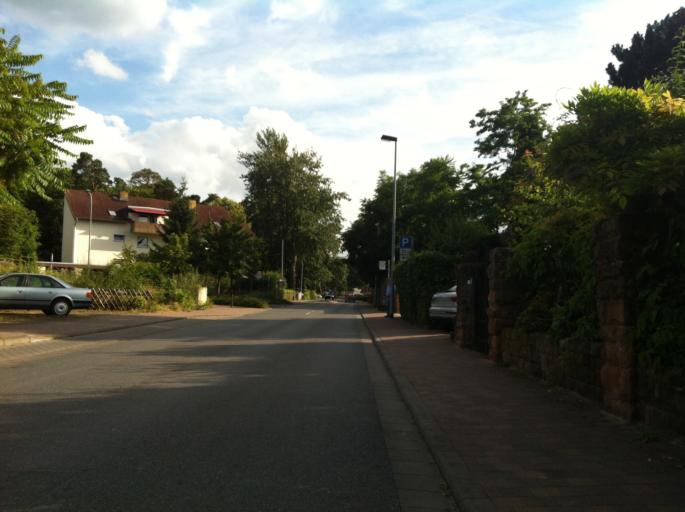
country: DE
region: Rheinland-Pfalz
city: Budenheim
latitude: 50.0189
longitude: 8.1687
